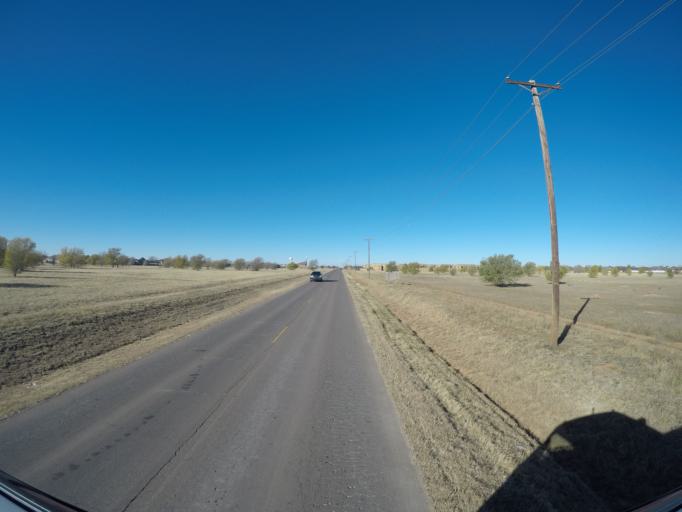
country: US
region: New Mexico
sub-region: Curry County
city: Clovis
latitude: 34.4339
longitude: -103.1704
